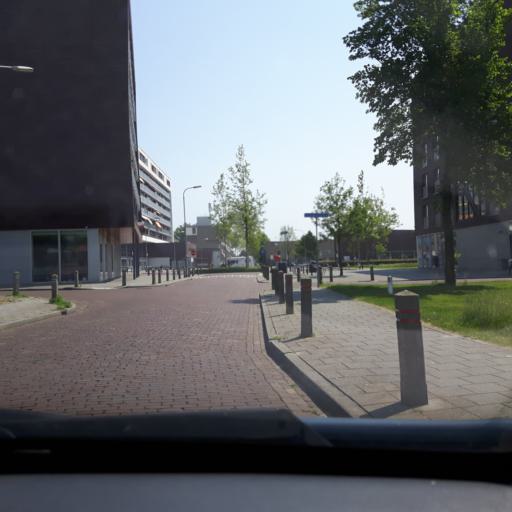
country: NL
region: Zeeland
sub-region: Gemeente Middelburg
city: Middelburg
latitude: 51.4865
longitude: 3.6167
